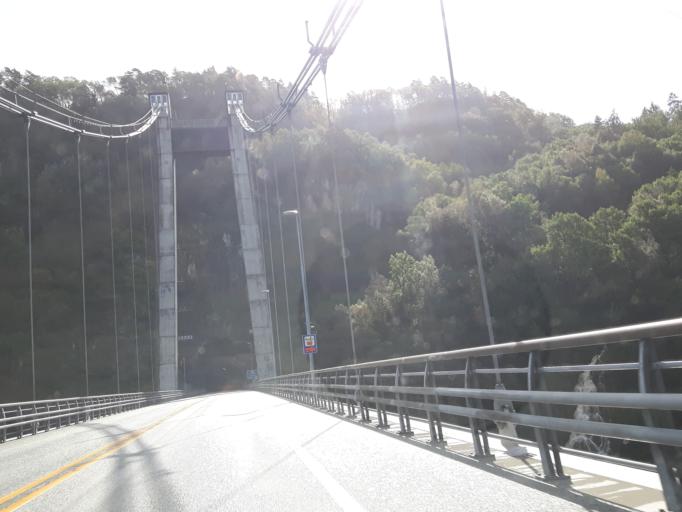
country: NO
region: Vest-Agder
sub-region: Kvinesdal
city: Liknes
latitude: 58.2609
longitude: 6.8462
